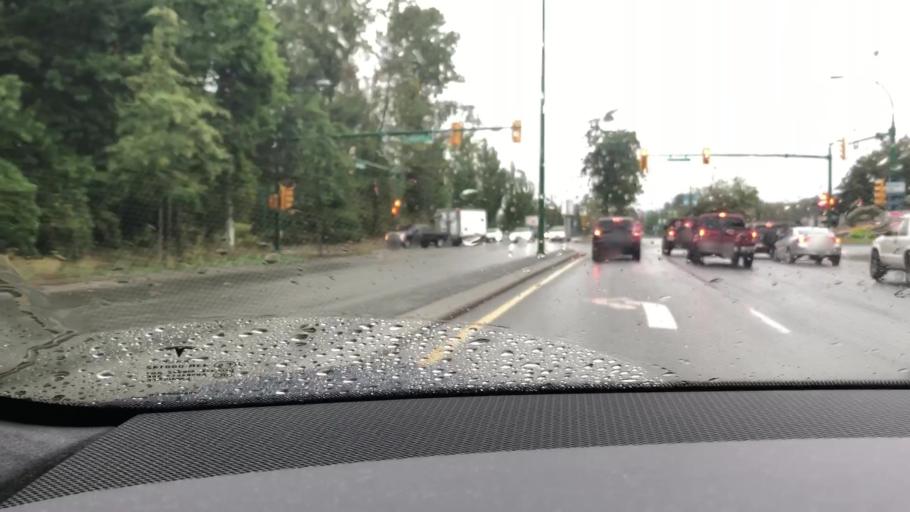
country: CA
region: British Columbia
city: Burnaby
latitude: 49.2485
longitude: -122.9680
